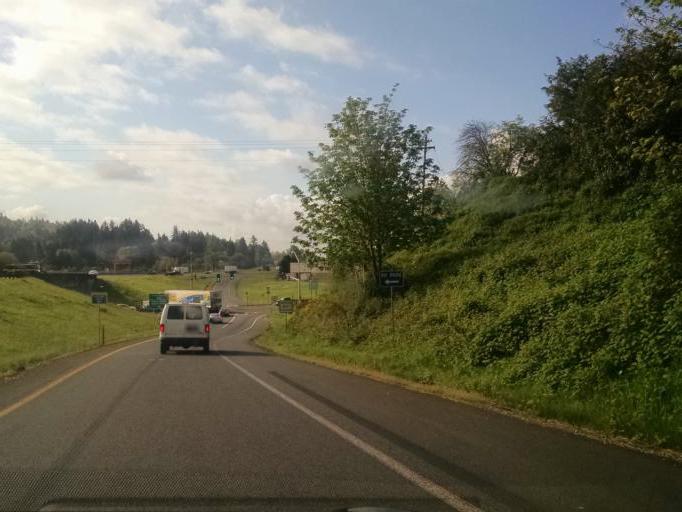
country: US
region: Washington
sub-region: Cowlitz County
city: Kelso
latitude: 46.1457
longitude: -122.8985
